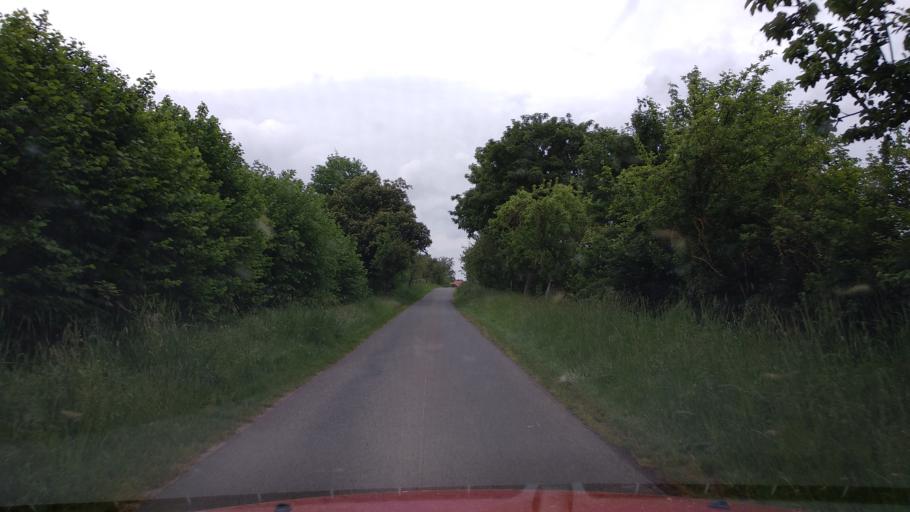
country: DE
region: North Rhine-Westphalia
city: Borgentreich
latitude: 51.5672
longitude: 9.1759
